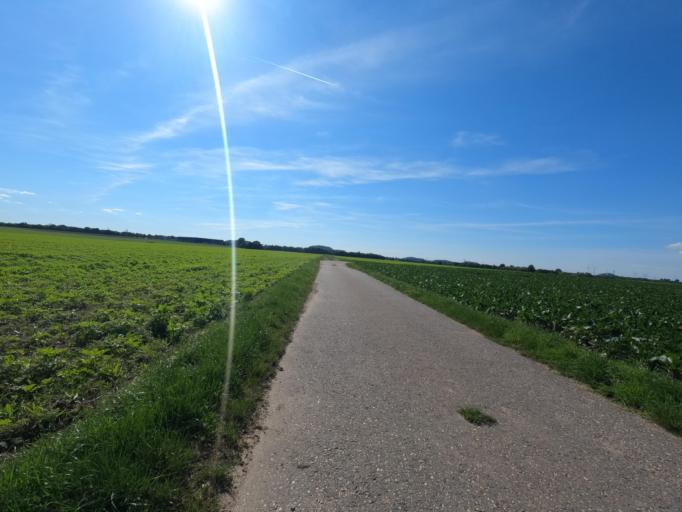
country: DE
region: North Rhine-Westphalia
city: Siersdorf
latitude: 50.8898
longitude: 6.2251
